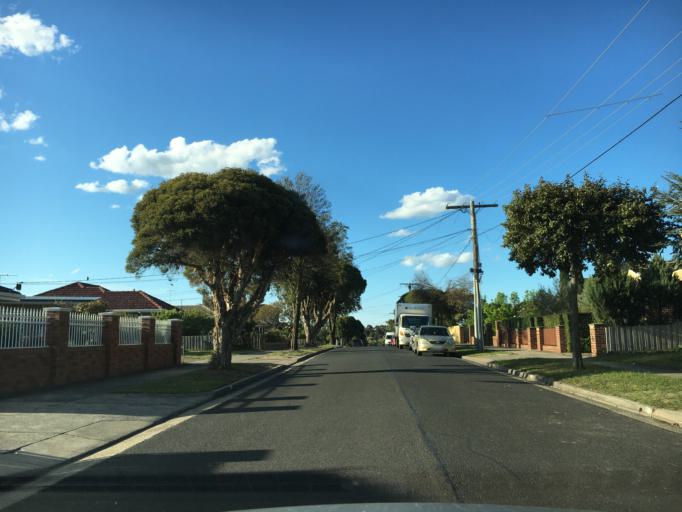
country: AU
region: Victoria
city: Clayton
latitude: -37.9041
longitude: 145.1201
